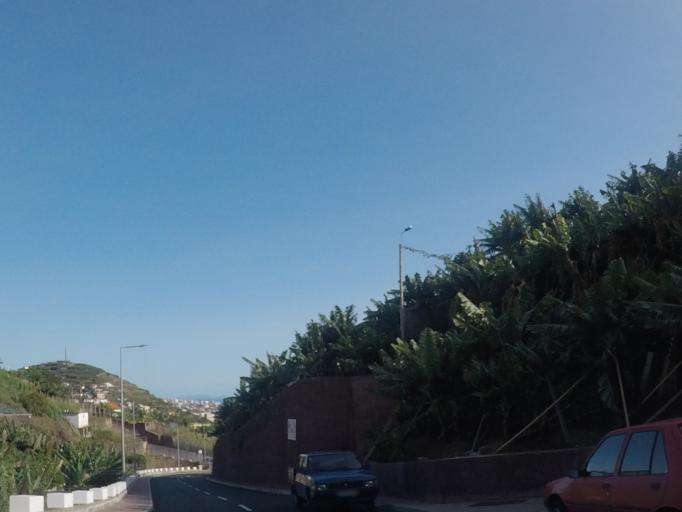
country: PT
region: Madeira
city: Camara de Lobos
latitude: 32.6552
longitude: -16.9877
